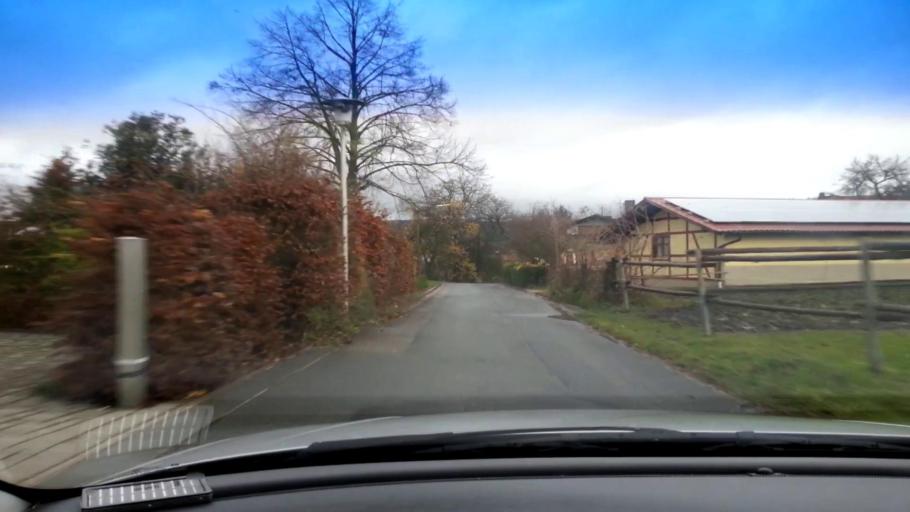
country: DE
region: Bavaria
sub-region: Upper Franconia
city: Ebensfeld
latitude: 50.0326
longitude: 11.0023
